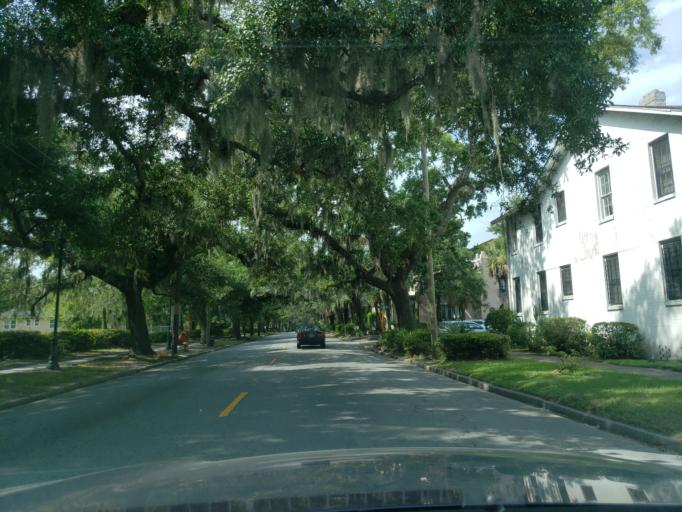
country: US
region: Georgia
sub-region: Chatham County
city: Thunderbolt
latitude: 32.0470
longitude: -81.0857
